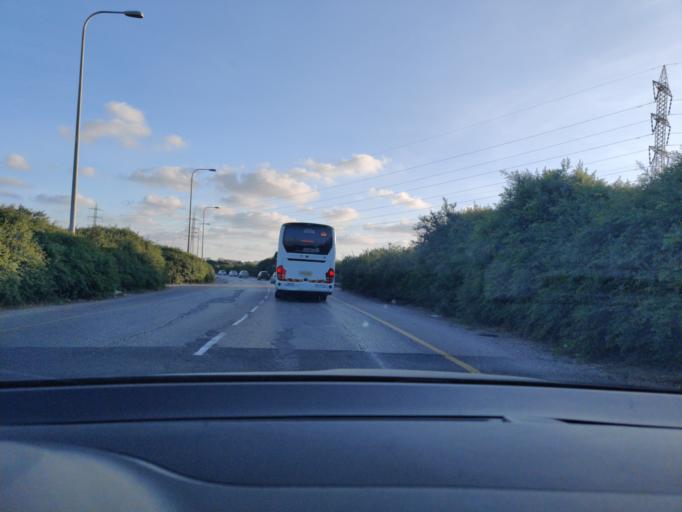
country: IL
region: Haifa
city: Hadera
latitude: 32.4465
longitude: 34.9406
